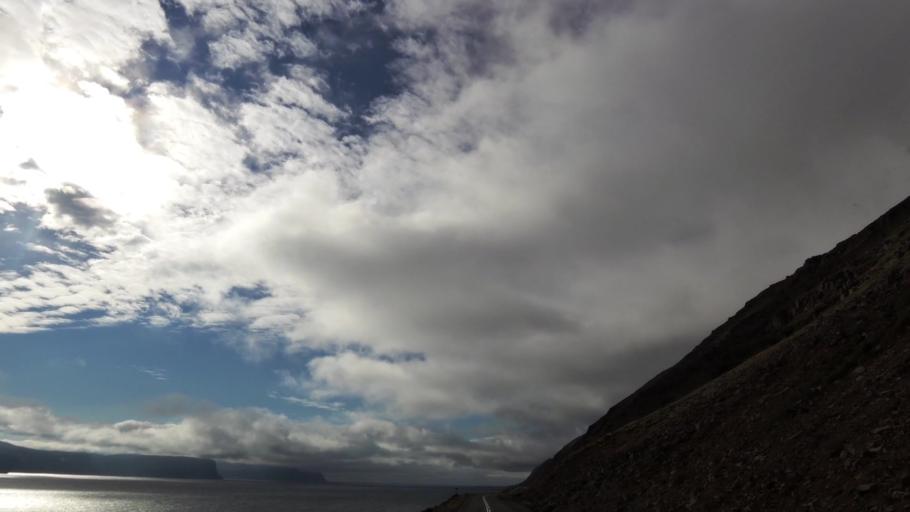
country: IS
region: West
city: Olafsvik
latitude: 65.5601
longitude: -23.9079
